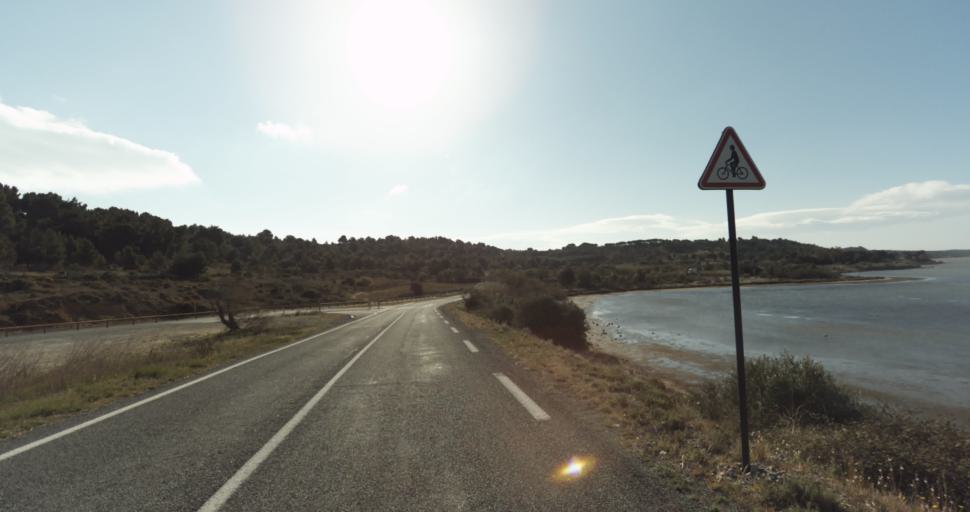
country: FR
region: Languedoc-Roussillon
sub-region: Departement de l'Aude
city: Leucate
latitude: 42.9282
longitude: 3.0116
